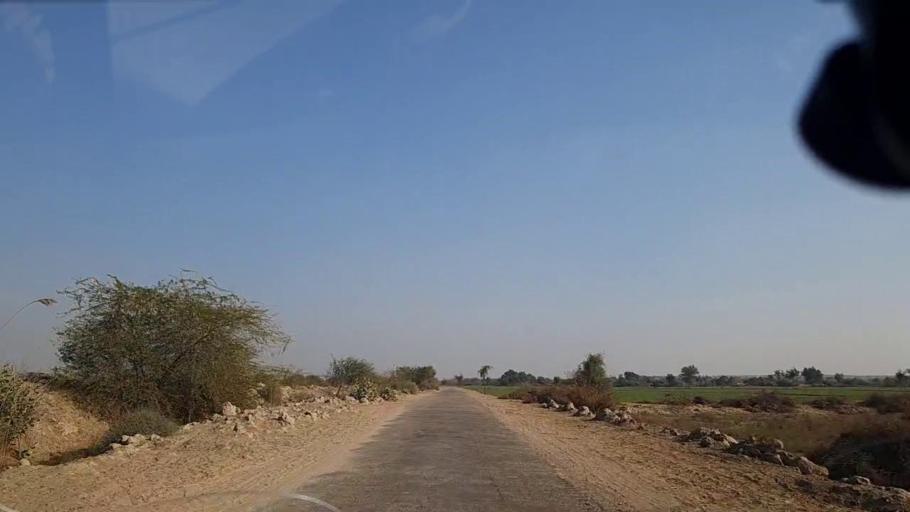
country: PK
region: Sindh
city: Khanpur
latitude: 27.6836
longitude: 69.5302
